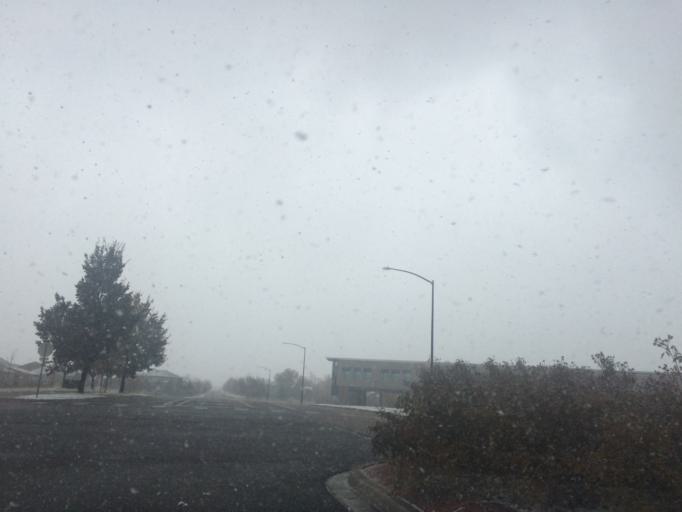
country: US
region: Colorado
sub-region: Boulder County
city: Erie
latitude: 40.0447
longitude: -105.0651
